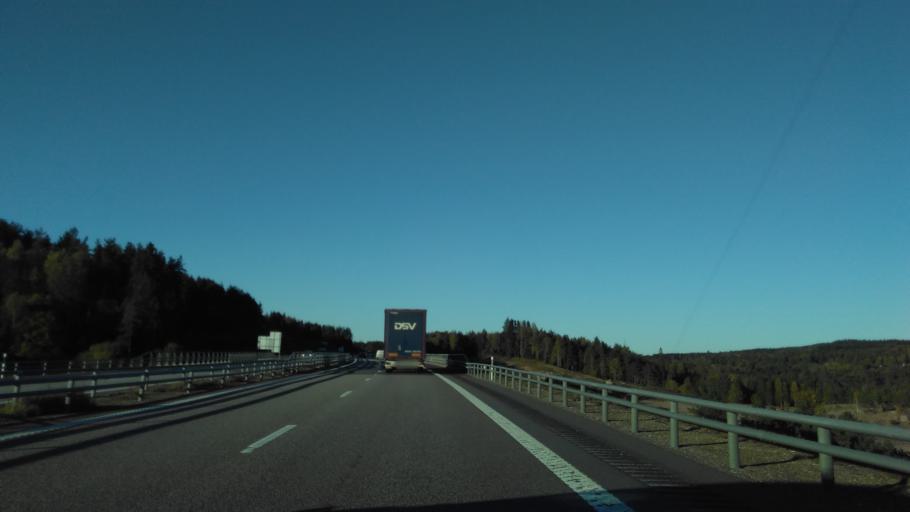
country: SE
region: Vaestra Goetaland
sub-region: Boras Kommun
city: Dalsjofors
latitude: 57.7652
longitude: 13.1115
